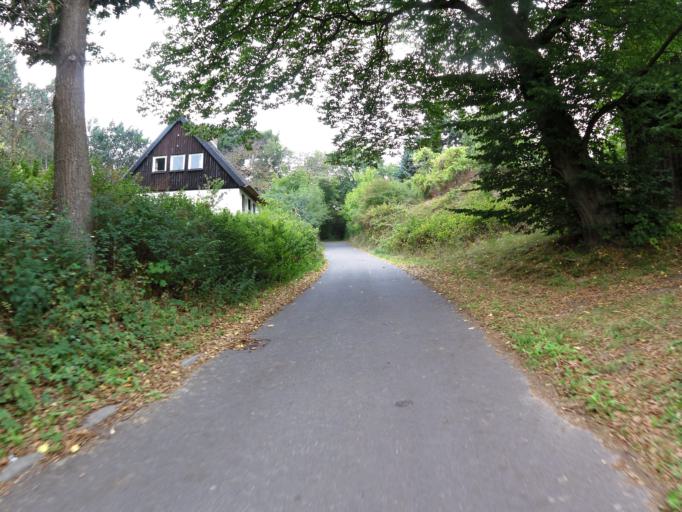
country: PL
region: West Pomeranian Voivodeship
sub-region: Swinoujscie
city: Swinoujscie
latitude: 53.8774
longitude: 14.2072
